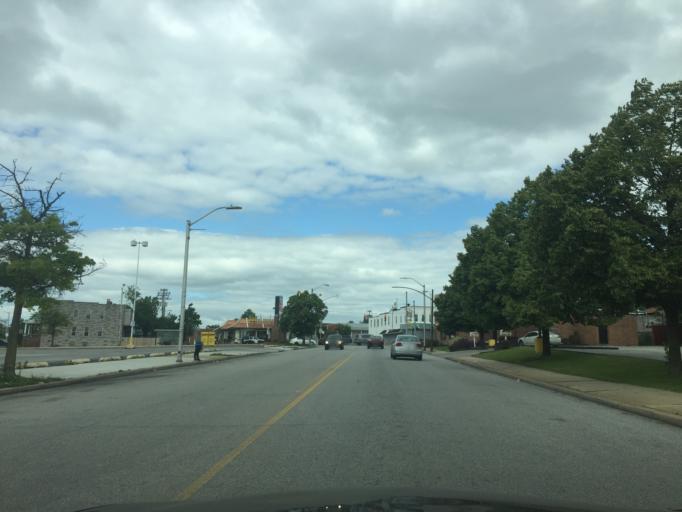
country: US
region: Maryland
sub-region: City of Baltimore
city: Baltimore
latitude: 39.3230
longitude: -76.6082
